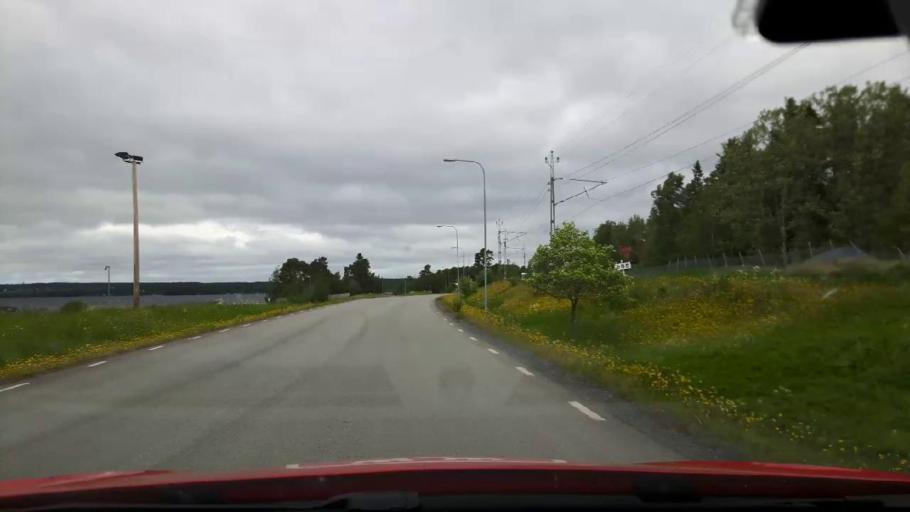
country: SE
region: Jaemtland
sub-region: OEstersunds Kommun
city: Ostersund
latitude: 63.1880
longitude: 14.6312
